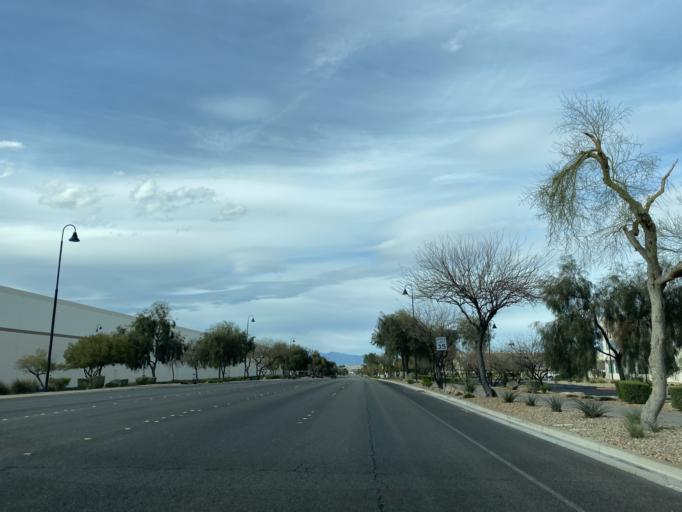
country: US
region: Nevada
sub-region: Clark County
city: Henderson
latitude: 36.0502
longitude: -115.0197
